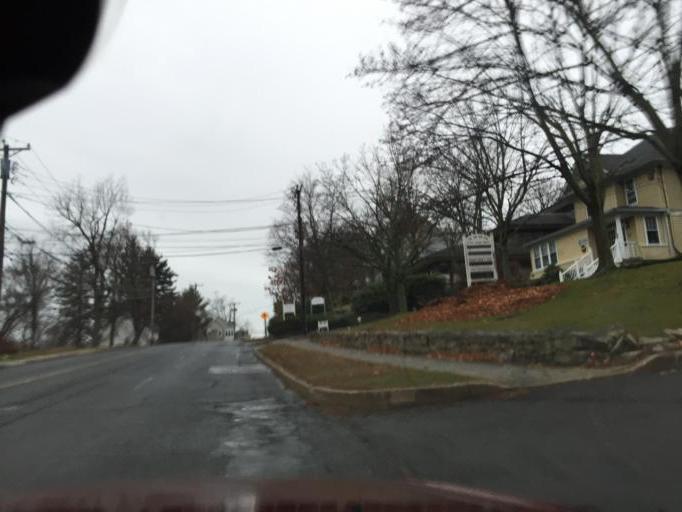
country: US
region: Connecticut
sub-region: Fairfield County
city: Westport
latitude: 41.1393
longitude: -73.3656
